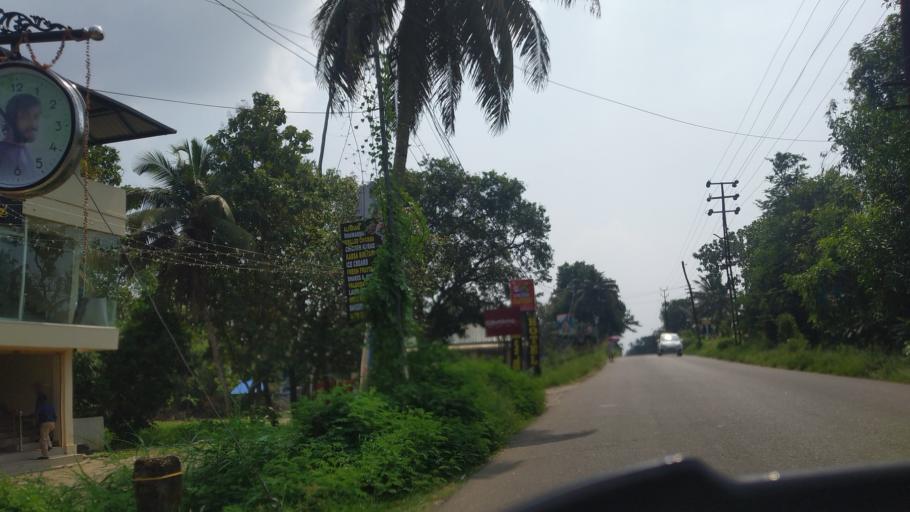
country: IN
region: Kerala
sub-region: Ernakulam
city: Elur
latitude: 10.0386
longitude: 76.2196
